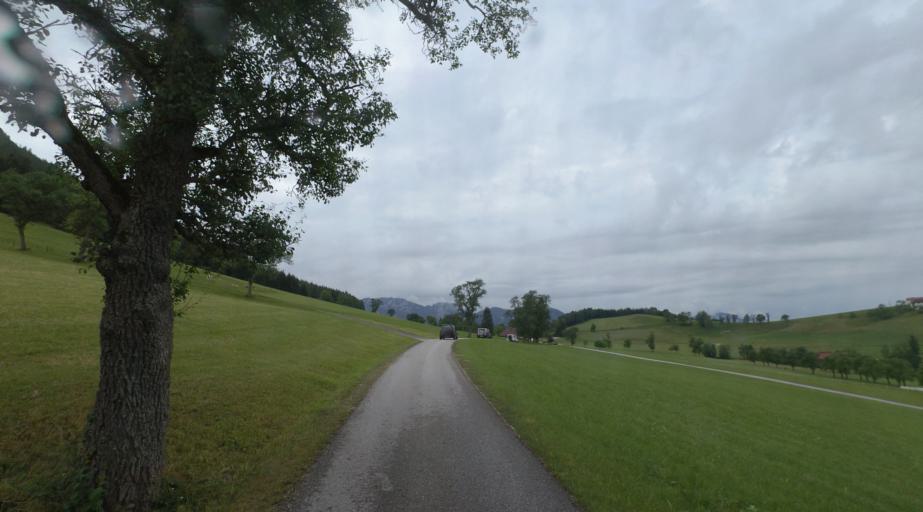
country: AT
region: Upper Austria
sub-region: Politischer Bezirk Kirchdorf an der Krems
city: Micheldorf in Oberoesterreich
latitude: 47.8946
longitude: 14.1663
